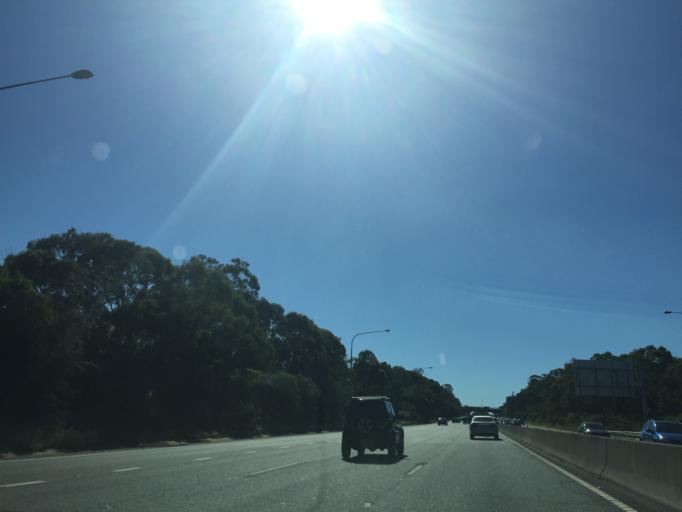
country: AU
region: New South Wales
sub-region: Holroyd
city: Girraween
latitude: -33.8149
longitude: 150.9584
